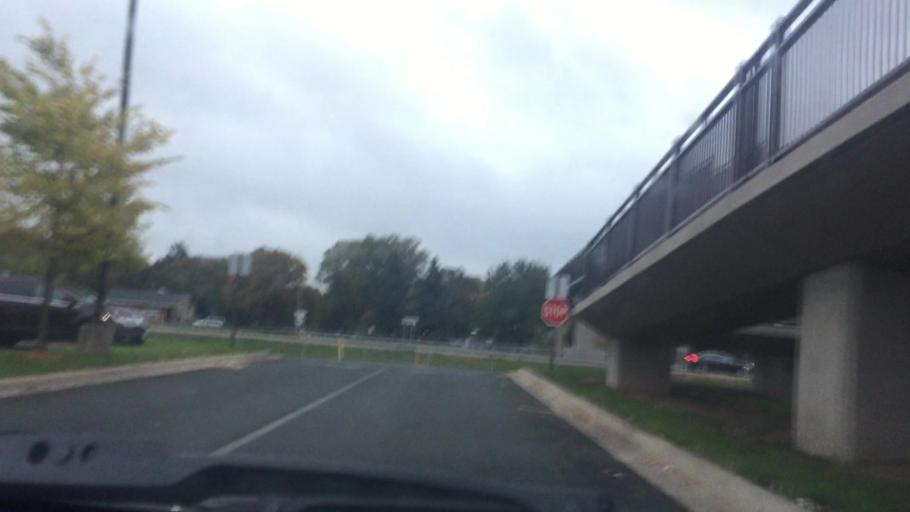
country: US
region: Minnesota
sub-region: Anoka County
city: Spring Lake Park
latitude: 45.1127
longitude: -93.2439
